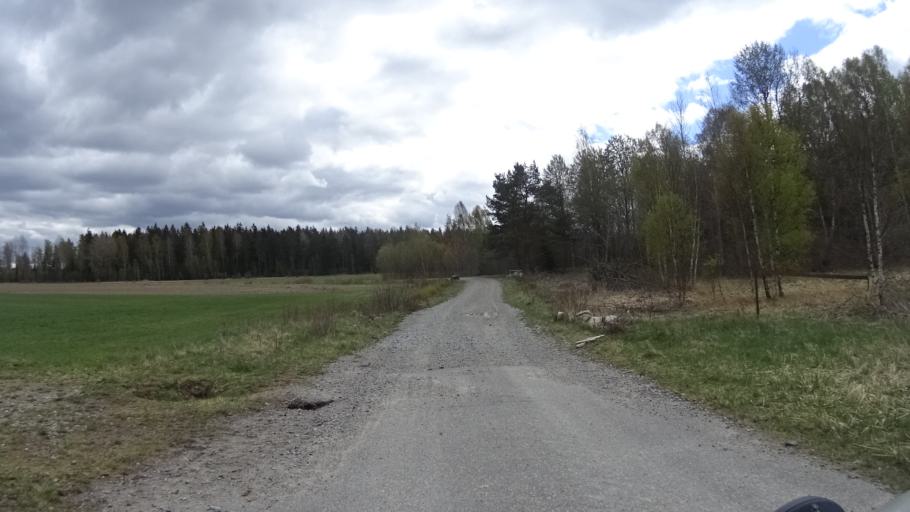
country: SE
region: Stockholm
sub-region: Botkyrka Kommun
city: Tullinge
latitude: 59.1768
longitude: 17.8995
